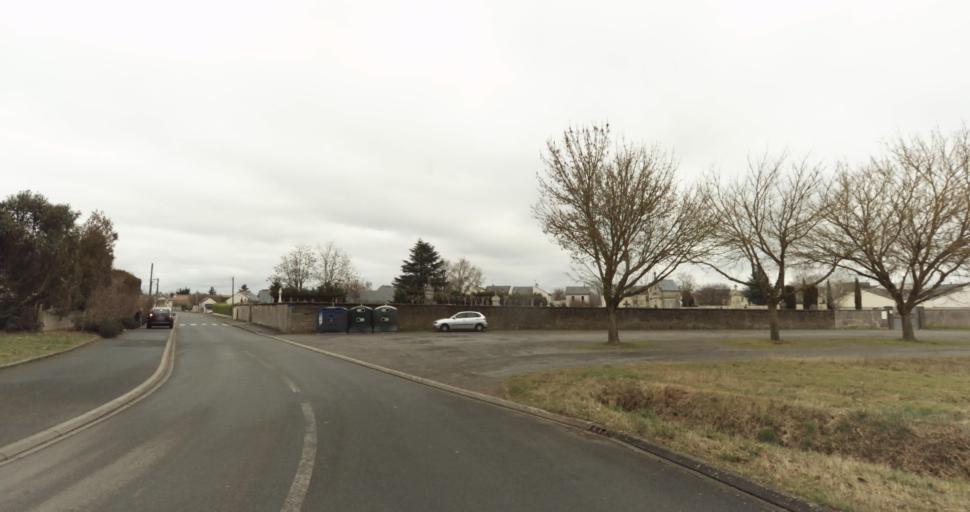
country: FR
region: Pays de la Loire
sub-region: Departement de Maine-et-Loire
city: Doue-la-Fontaine
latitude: 47.1832
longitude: -0.2639
